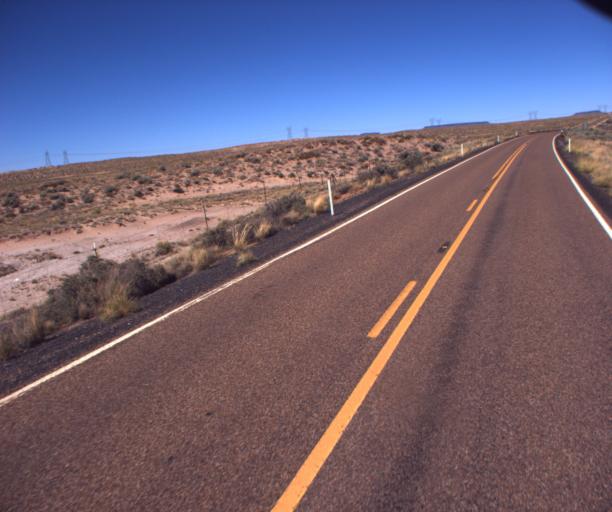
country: US
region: Arizona
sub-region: Navajo County
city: Holbrook
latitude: 35.1418
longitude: -110.0895
